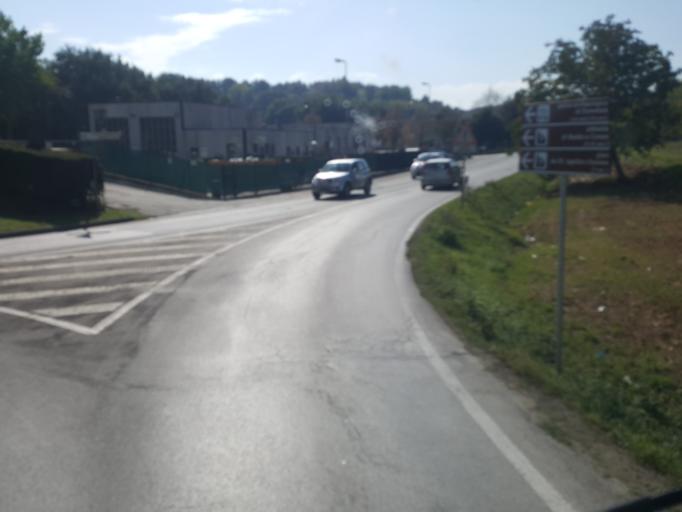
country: IT
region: Tuscany
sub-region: Provincia di Siena
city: Colle di Val d'Elsa
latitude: 43.4150
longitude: 11.1284
